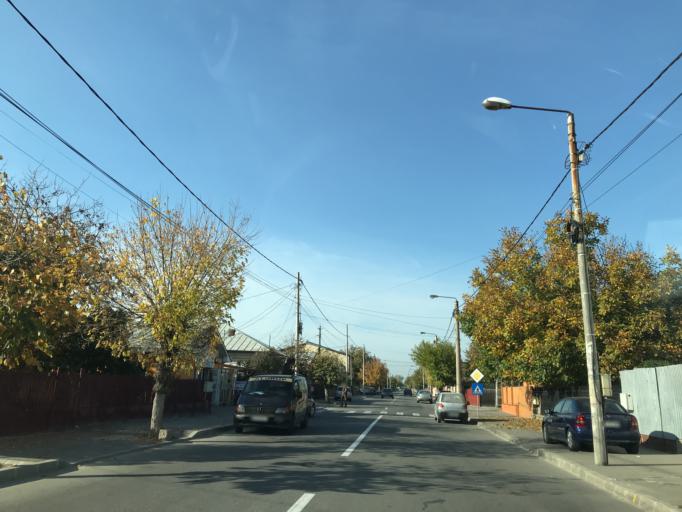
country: RO
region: Olt
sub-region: Municipiul Slatina
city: Slatina
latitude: 44.4339
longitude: 24.3511
